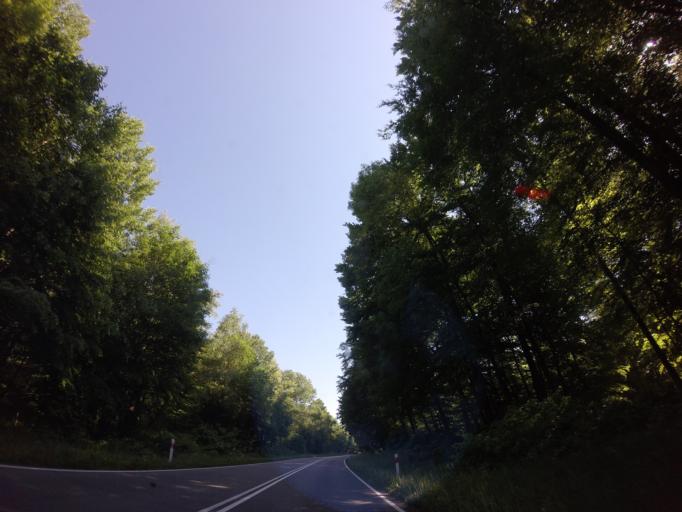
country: PL
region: West Pomeranian Voivodeship
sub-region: Powiat gryfinski
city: Stare Czarnowo
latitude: 53.3200
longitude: 14.7906
